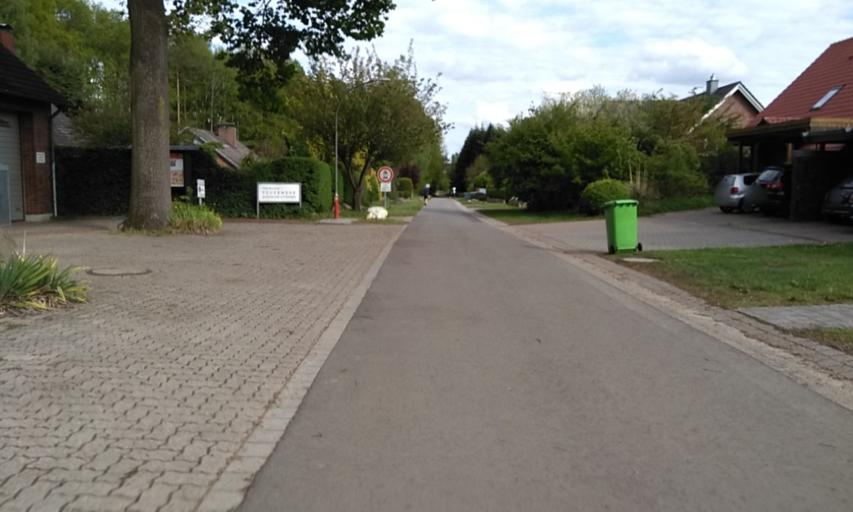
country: DE
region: Lower Saxony
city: Buxtehude
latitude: 53.4496
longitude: 9.6702
